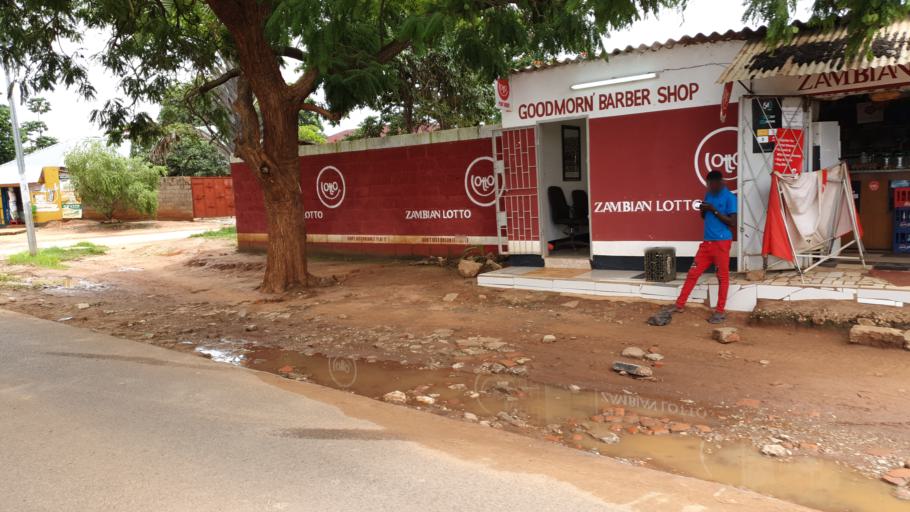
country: ZM
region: Lusaka
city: Lusaka
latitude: -15.4294
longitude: 28.3063
